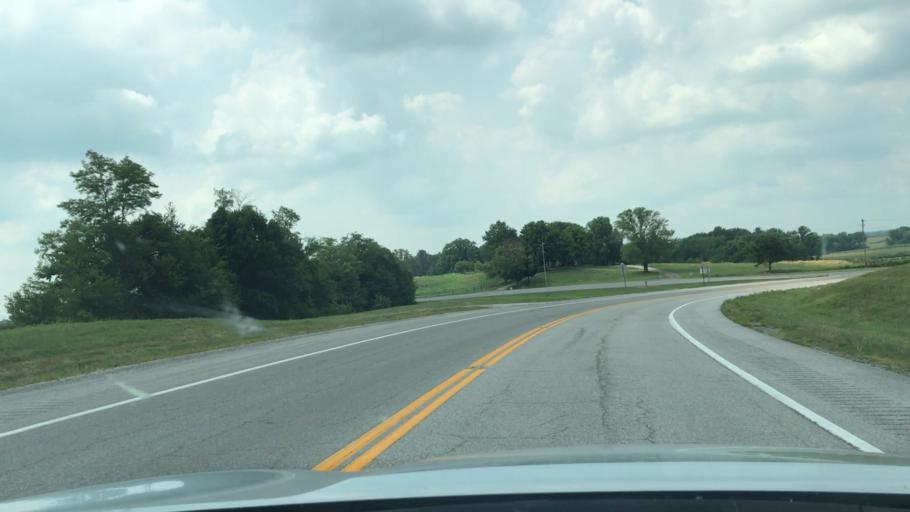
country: US
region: Kentucky
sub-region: Todd County
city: Elkton
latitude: 36.8063
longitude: -87.1208
